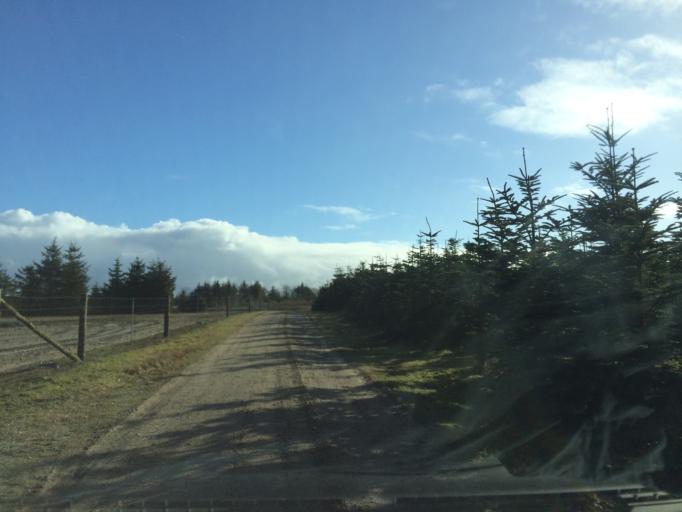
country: DK
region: Central Jutland
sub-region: Holstebro Kommune
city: Ulfborg
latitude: 56.2668
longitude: 8.4106
